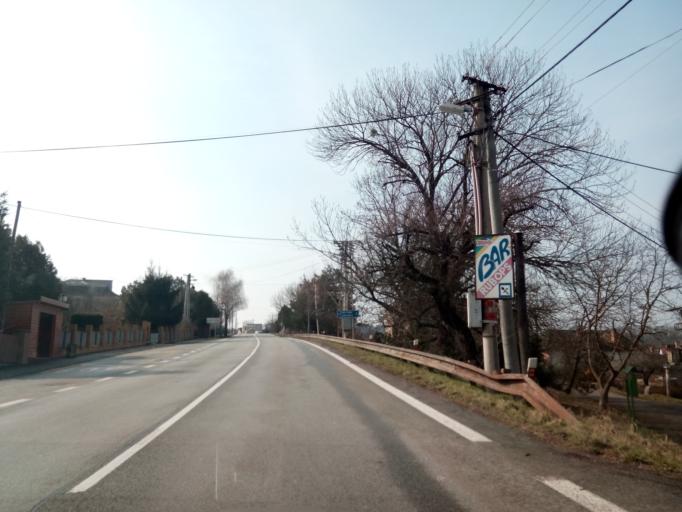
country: SK
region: Kosicky
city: Trebisov
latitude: 48.5231
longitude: 21.6632
